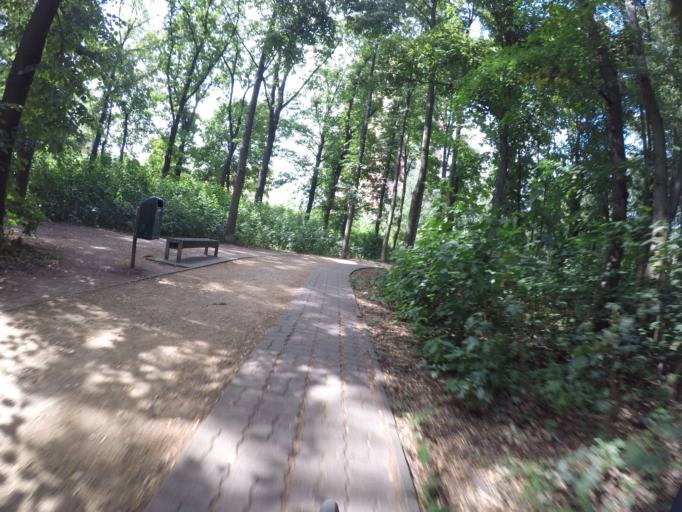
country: DE
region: Berlin
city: Marienfelde
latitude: 52.4113
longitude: 13.3511
